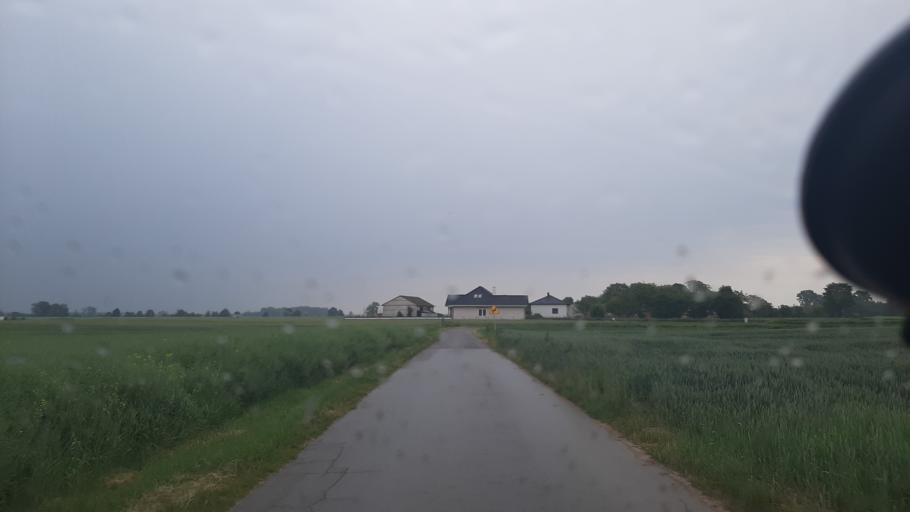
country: PL
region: Lublin Voivodeship
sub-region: Powiat lubelski
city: Garbow
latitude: 51.3524
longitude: 22.3564
